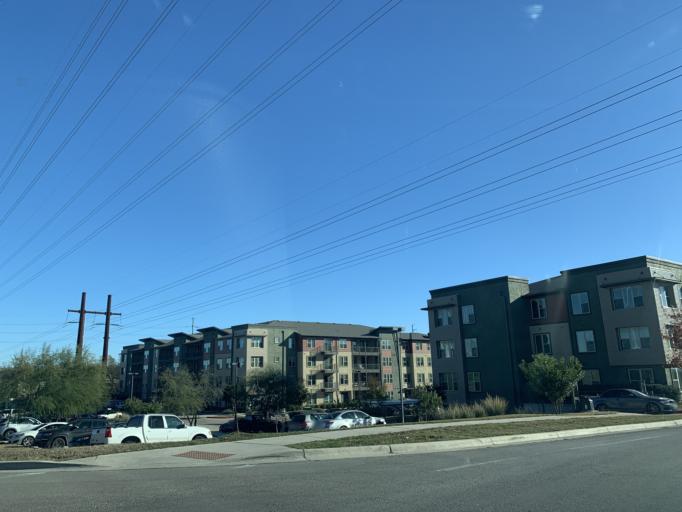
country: US
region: Texas
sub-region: Travis County
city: Wells Branch
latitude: 30.3973
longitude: -97.7172
